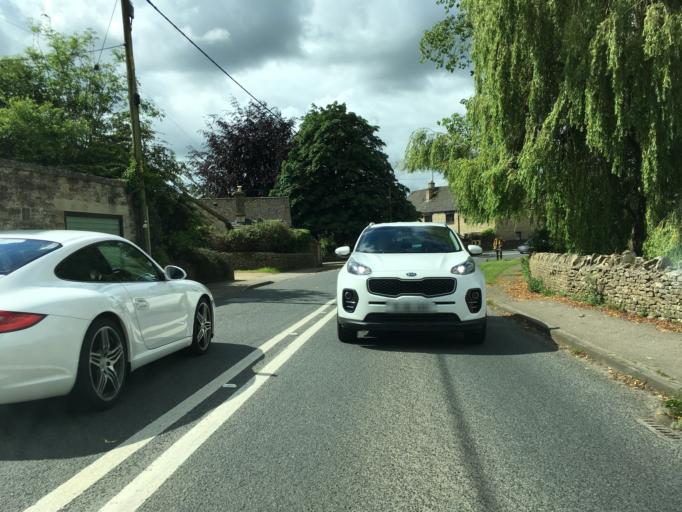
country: GB
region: England
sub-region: Oxfordshire
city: Burford
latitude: 51.8152
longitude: -1.6250
